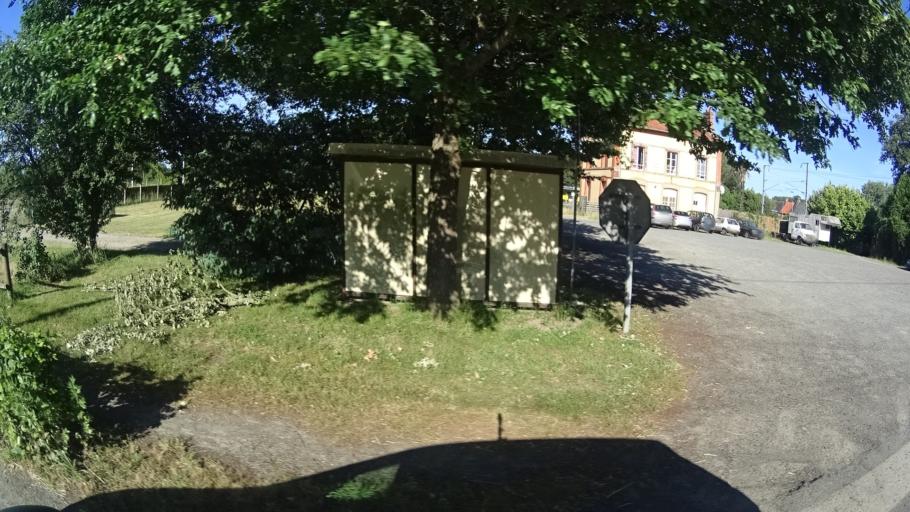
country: FR
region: Brittany
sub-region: Departement d'Ille-et-Vilaine
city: Langon
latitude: 47.7298
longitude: -1.8518
